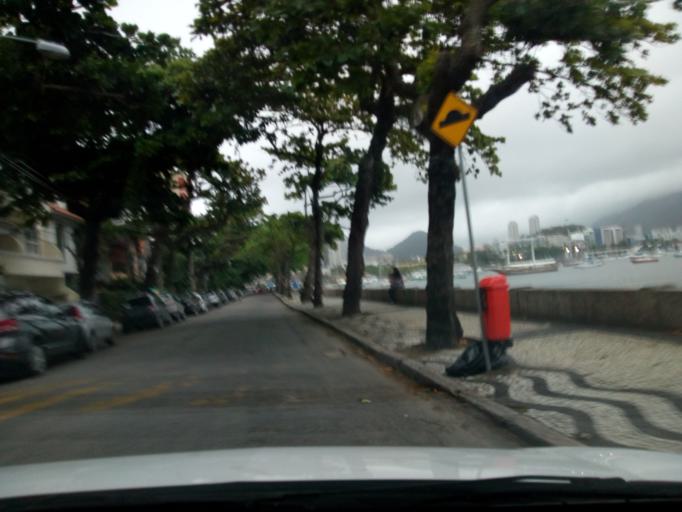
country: BR
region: Rio de Janeiro
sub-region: Rio De Janeiro
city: Rio de Janeiro
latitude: -22.9488
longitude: -43.1662
